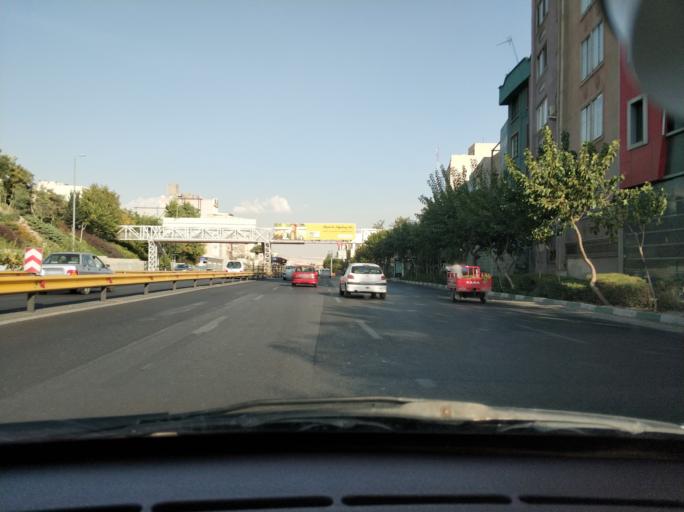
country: IR
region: Tehran
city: Tehran
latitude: 35.7426
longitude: 51.4377
